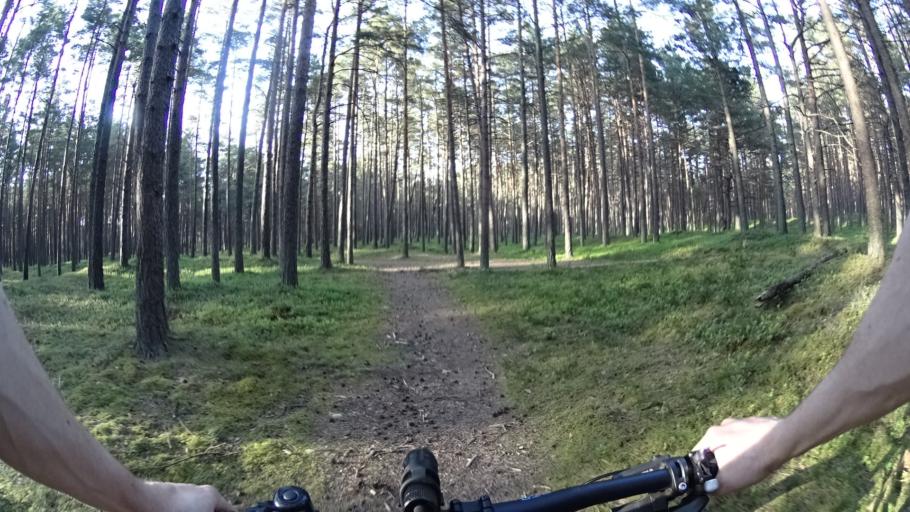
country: LV
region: Riga
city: Jaunciems
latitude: 57.0921
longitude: 24.1571
